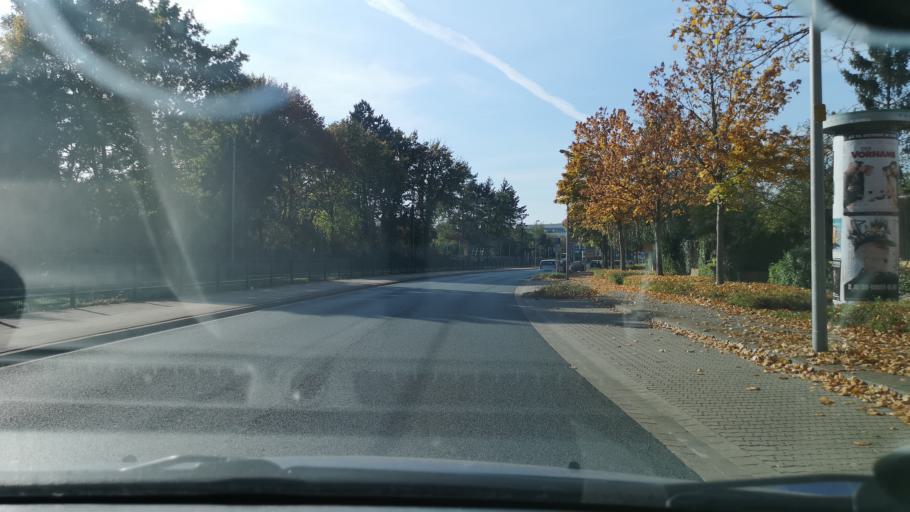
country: DE
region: Lower Saxony
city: Auf der Horst
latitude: 52.4170
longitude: 9.6130
